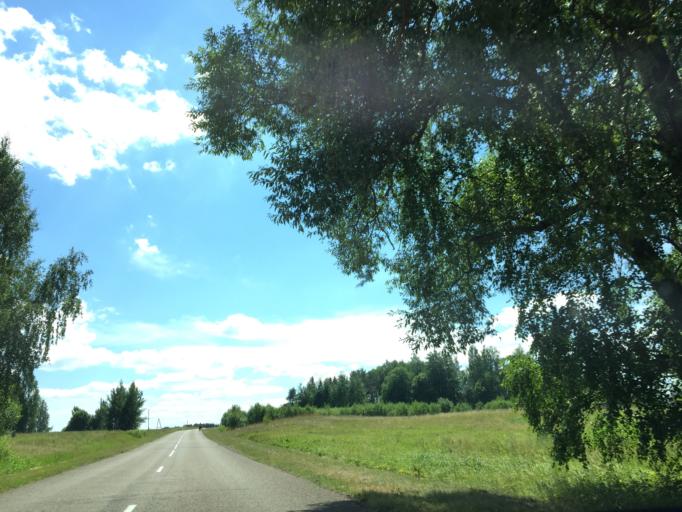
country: LV
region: Dagda
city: Dagda
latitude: 56.3058
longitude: 27.5130
